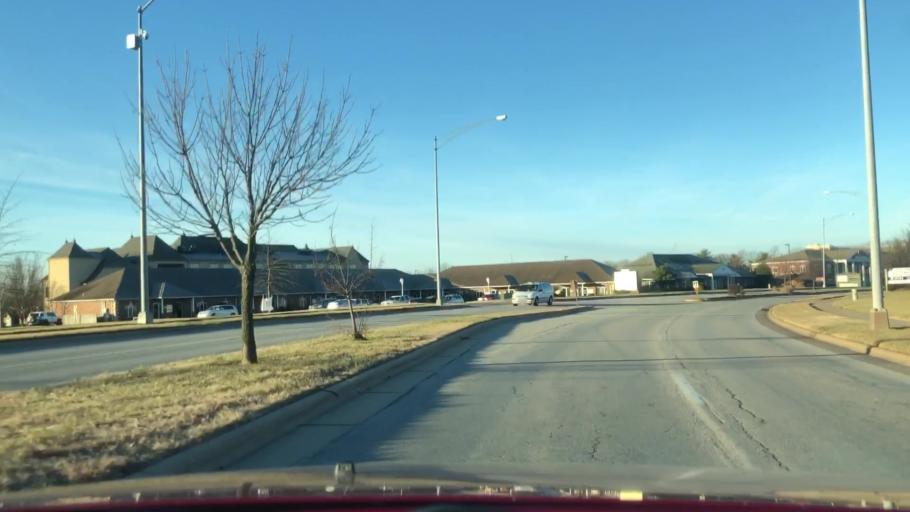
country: US
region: Missouri
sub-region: Greene County
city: Springfield
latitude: 37.1472
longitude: -93.2670
